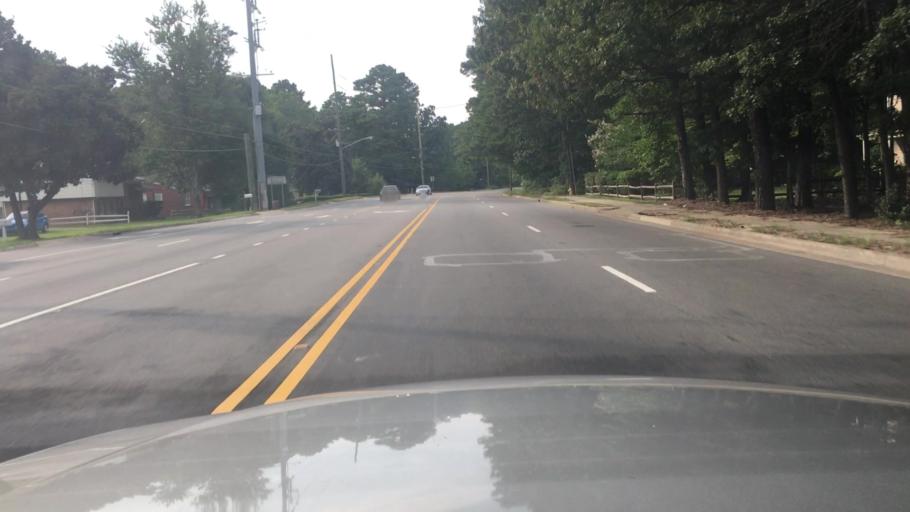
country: US
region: North Carolina
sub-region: Cumberland County
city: Fayetteville
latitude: 35.0607
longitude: -78.9489
